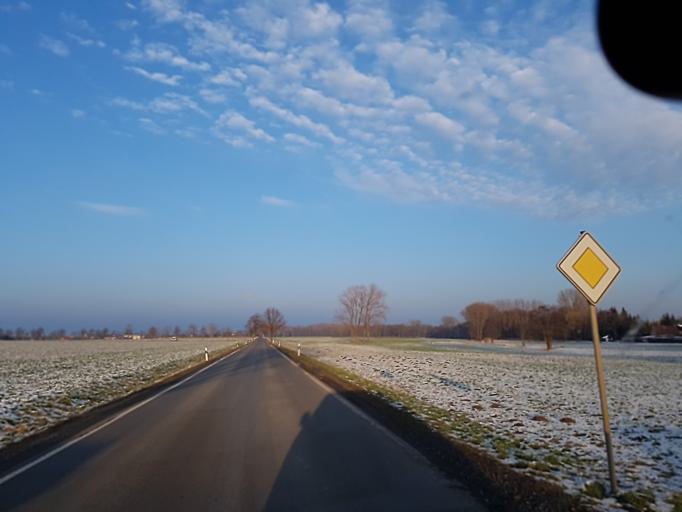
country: DE
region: Saxony
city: Oschatz
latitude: 51.3036
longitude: 13.1686
